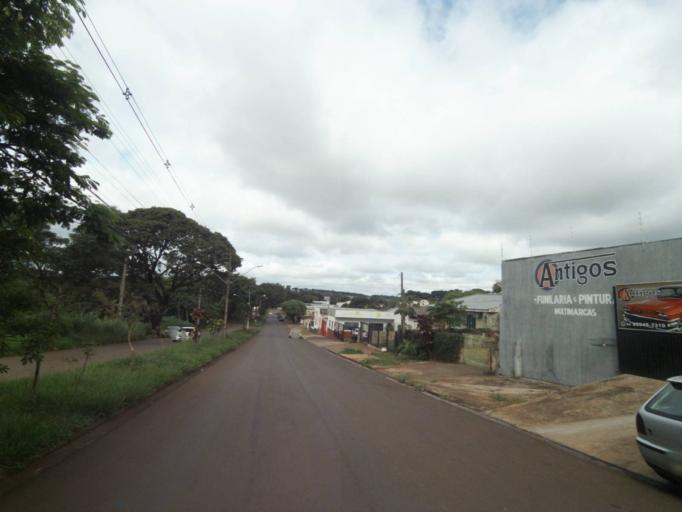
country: BR
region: Parana
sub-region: Campo Mourao
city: Campo Mourao
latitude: -24.0517
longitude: -52.3803
